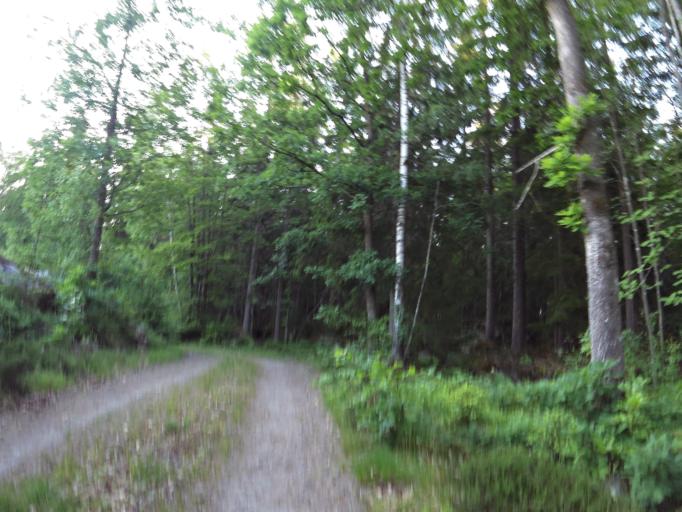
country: SE
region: Blekinge
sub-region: Olofstroms Kommun
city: Olofstroem
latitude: 56.4128
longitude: 14.5573
